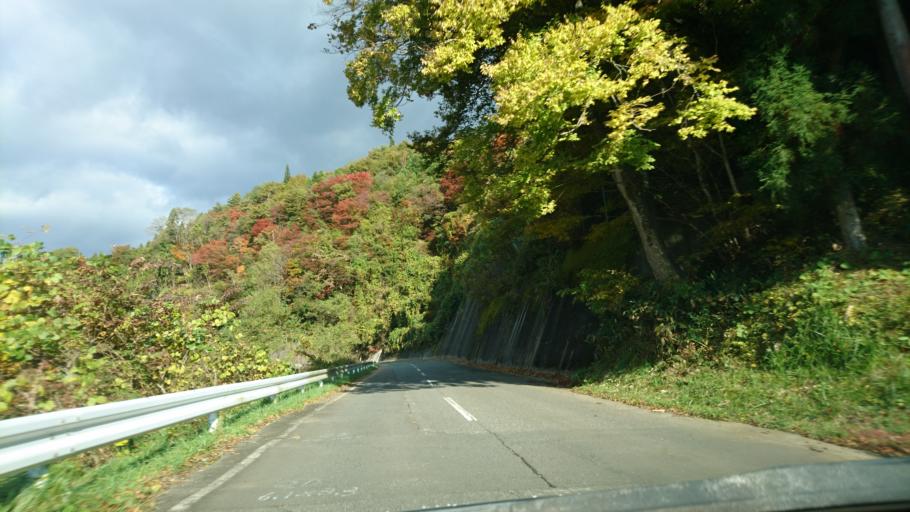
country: JP
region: Iwate
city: Mizusawa
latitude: 39.0833
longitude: 140.9972
